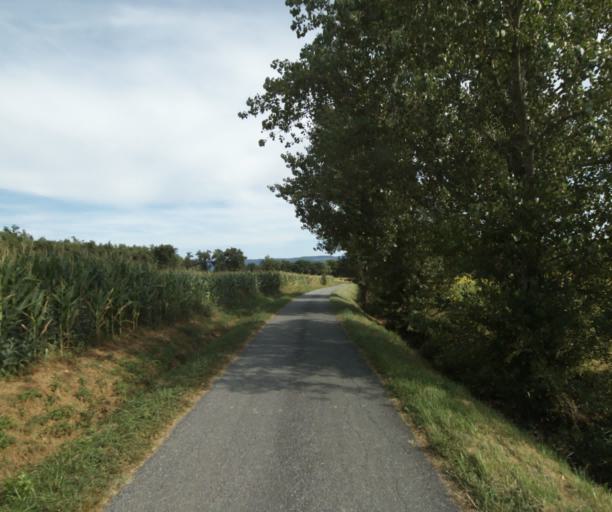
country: FR
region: Midi-Pyrenees
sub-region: Departement du Tarn
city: Puylaurens
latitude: 43.5309
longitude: 2.0455
